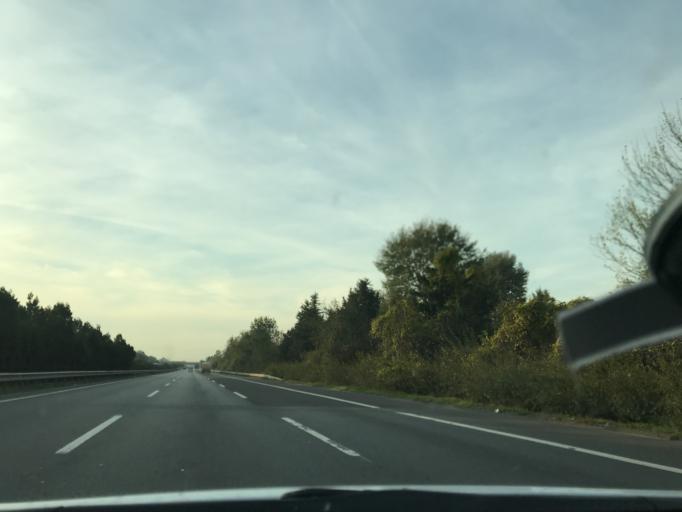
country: TR
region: Duzce
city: Cilimli
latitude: 40.8232
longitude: 31.0638
